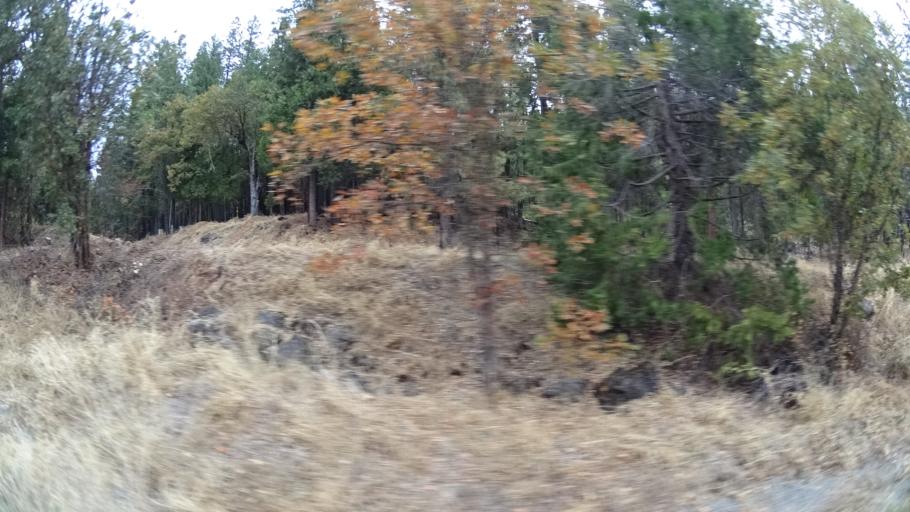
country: US
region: California
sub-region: Siskiyou County
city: Happy Camp
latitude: 41.8743
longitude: -123.4118
